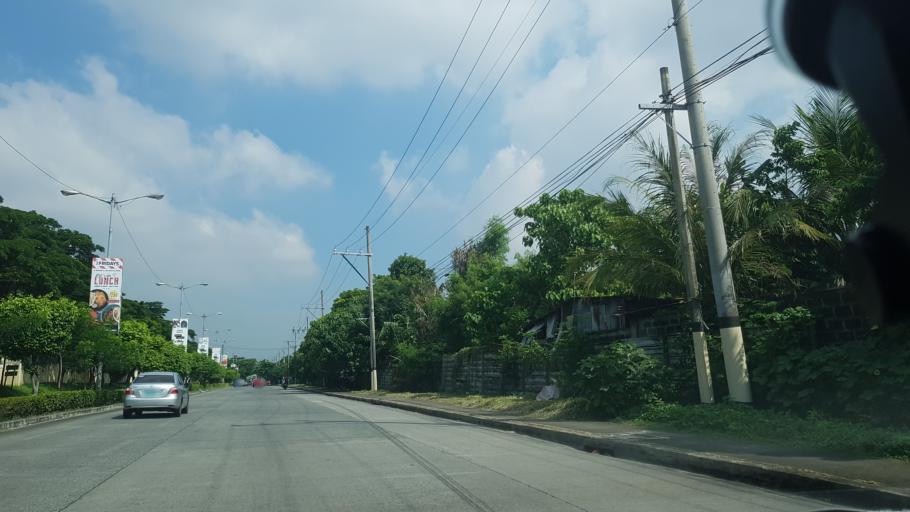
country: PH
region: Calabarzon
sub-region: Province of Laguna
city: San Pedro
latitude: 14.3810
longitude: 121.0130
